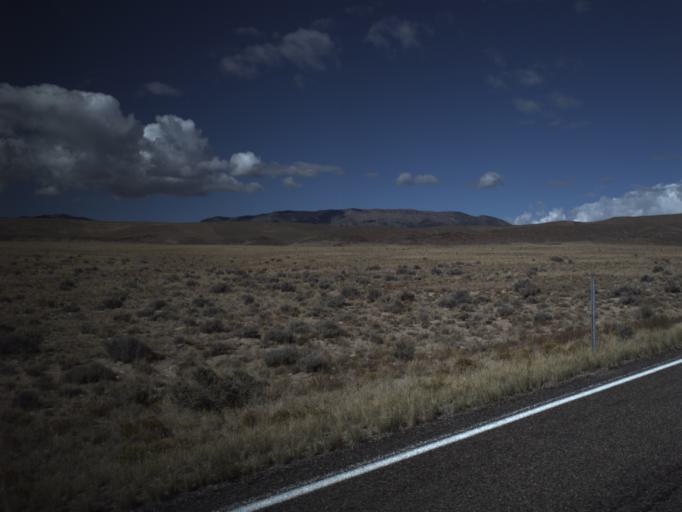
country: US
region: Utah
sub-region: Beaver County
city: Milford
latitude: 38.5863
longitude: -113.8147
